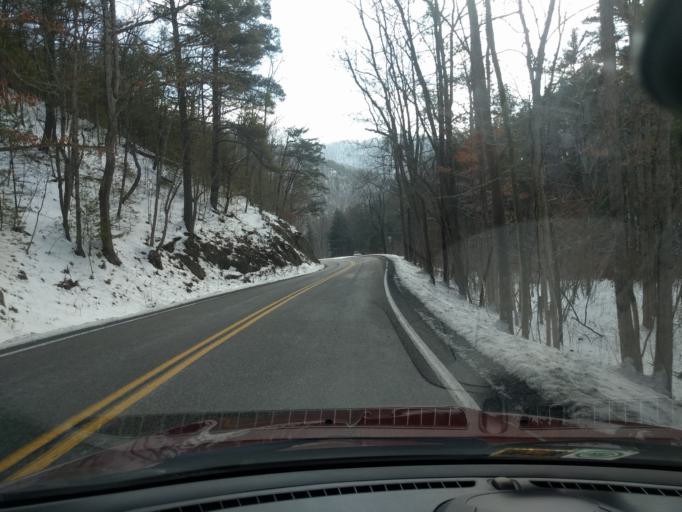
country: US
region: Virginia
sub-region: Bath County
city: Warm Springs
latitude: 38.1233
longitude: -79.9192
